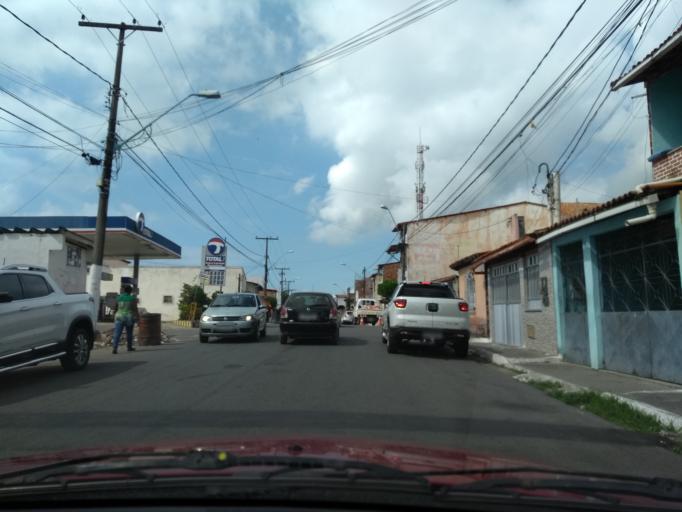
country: BR
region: Bahia
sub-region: Sao Francisco Do Conde
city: Sao Francisco do Conde
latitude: -12.6248
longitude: -38.6752
